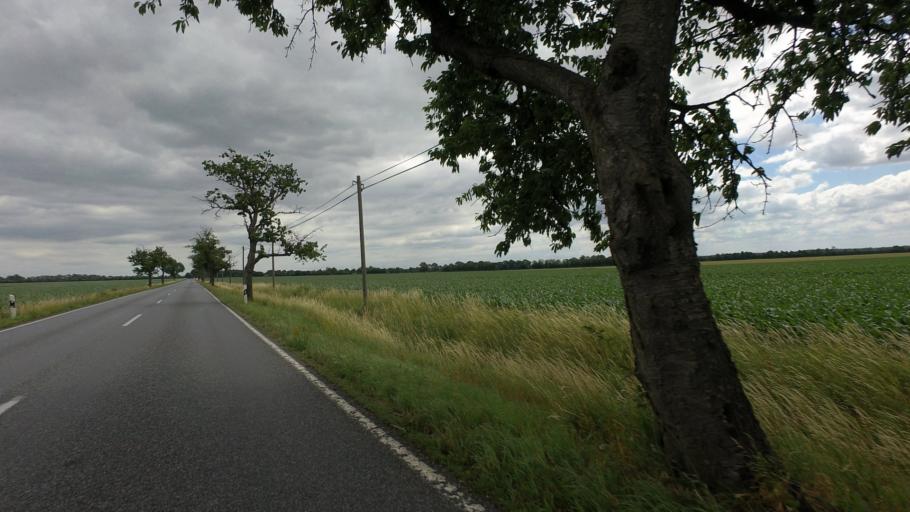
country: DE
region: Brandenburg
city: Luckau
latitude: 51.8285
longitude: 13.7803
